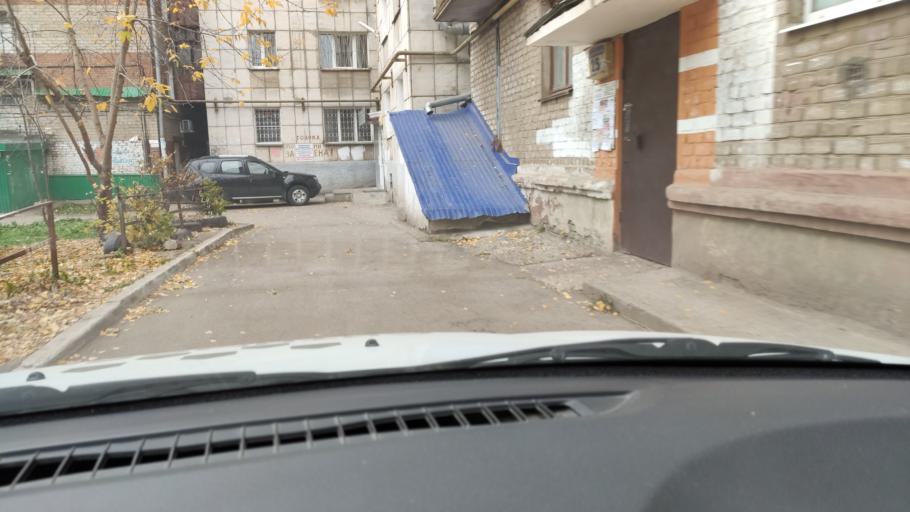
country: RU
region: Perm
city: Perm
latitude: 58.0105
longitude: 56.2828
